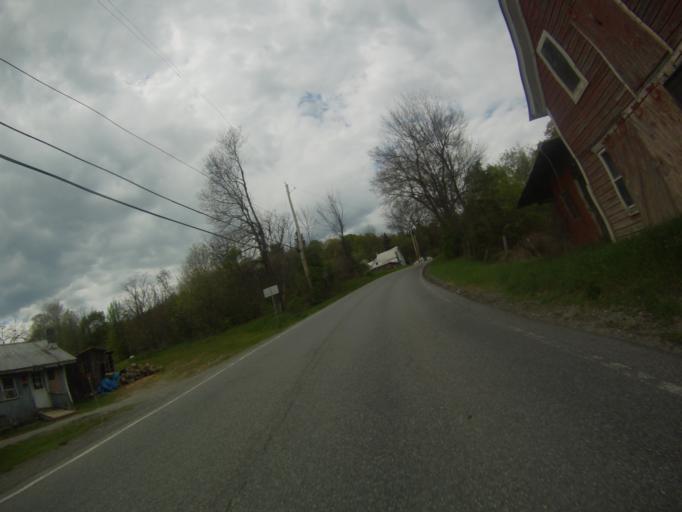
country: US
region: New York
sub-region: Essex County
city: Port Henry
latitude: 43.9598
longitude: -73.4886
